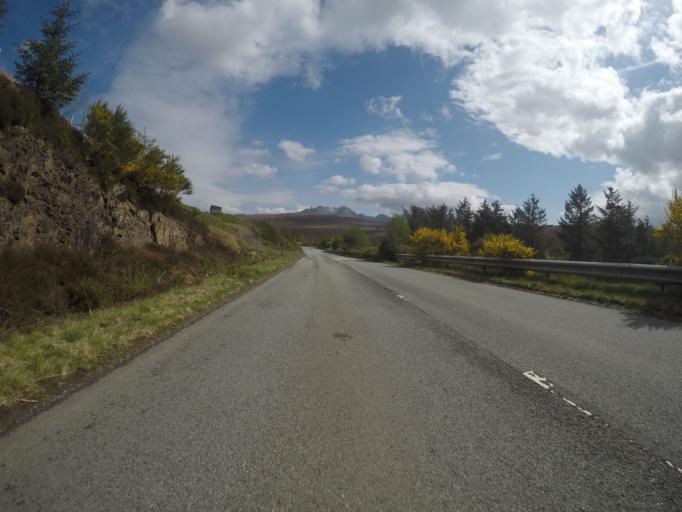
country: GB
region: Scotland
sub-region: Highland
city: Isle of Skye
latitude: 57.2999
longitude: -6.2945
